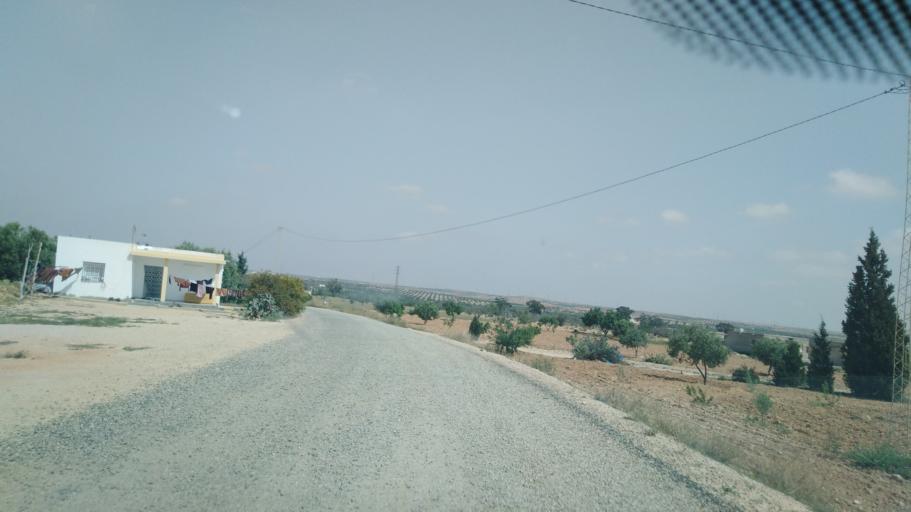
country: TN
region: Safaqis
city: Sfax
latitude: 34.7264
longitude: 10.5728
